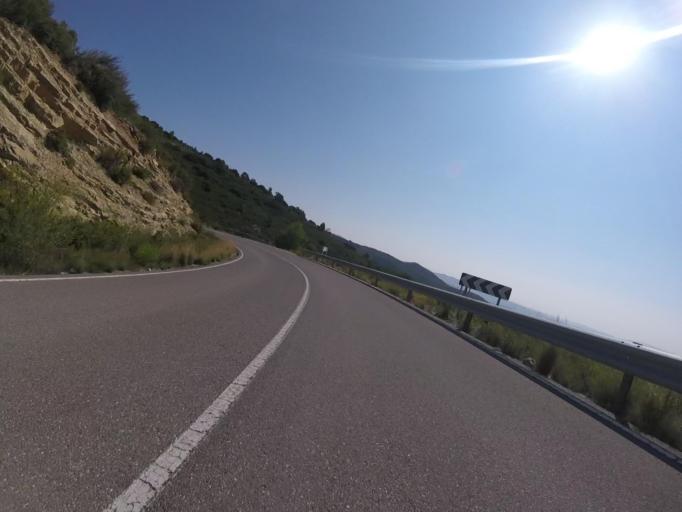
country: ES
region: Valencia
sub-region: Provincia de Castello
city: Benafigos
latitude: 40.2640
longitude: -0.2241
